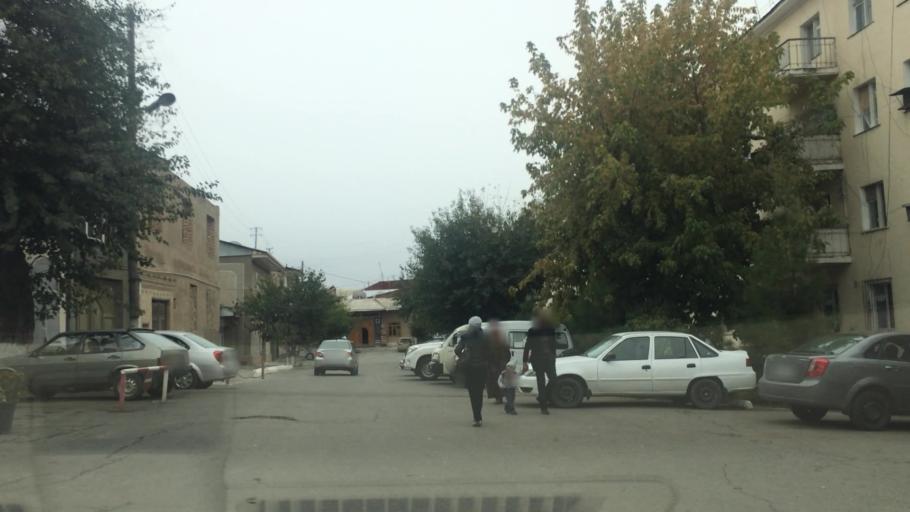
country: UZ
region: Samarqand
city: Samarqand
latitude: 39.6531
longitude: 66.9760
